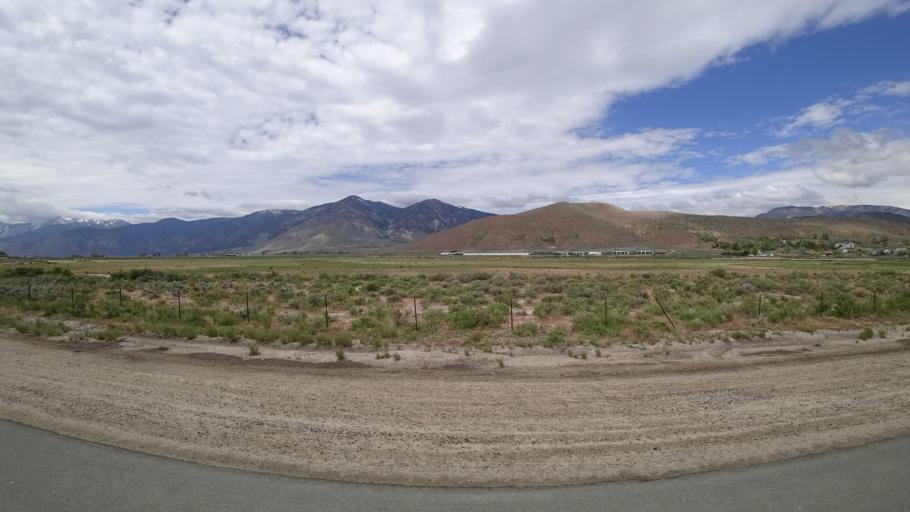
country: US
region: Nevada
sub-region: Douglas County
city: Indian Hills
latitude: 39.0635
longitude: -119.7802
